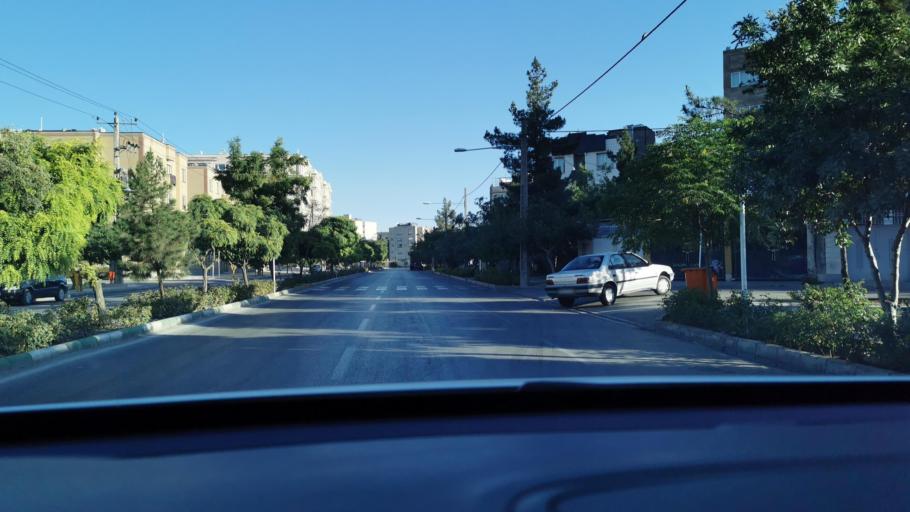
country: IR
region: Razavi Khorasan
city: Mashhad
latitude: 36.3587
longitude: 59.4851
